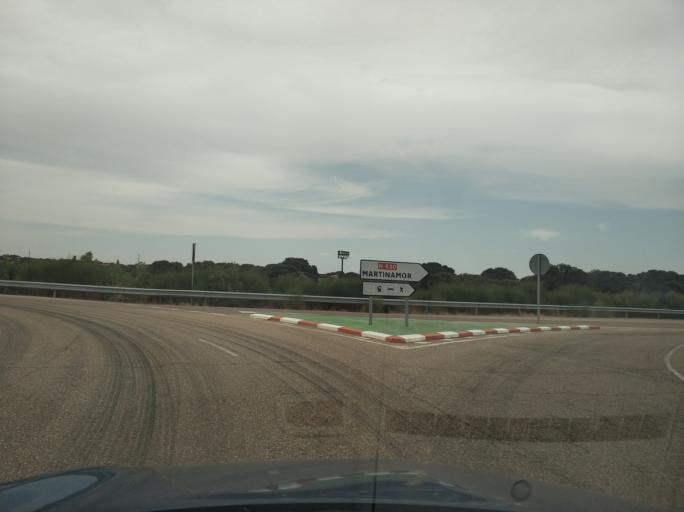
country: ES
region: Castille and Leon
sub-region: Provincia de Salamanca
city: Martinamor
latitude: 40.7998
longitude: -5.6363
